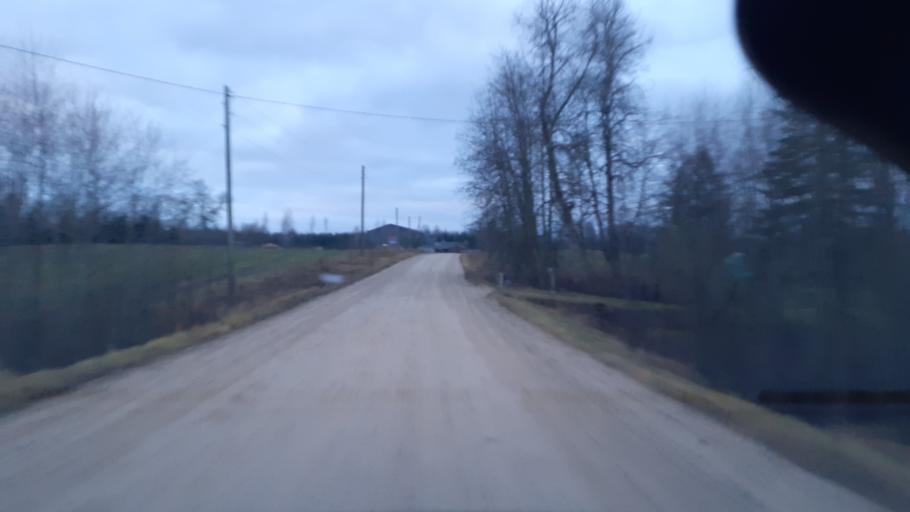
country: LV
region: Kuldigas Rajons
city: Kuldiga
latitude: 56.9525
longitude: 21.7886
